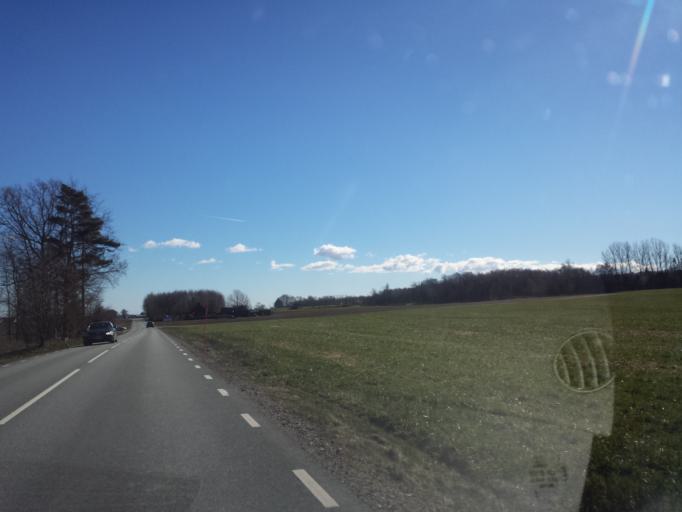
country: SE
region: Skane
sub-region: Sjobo Kommun
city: Sjoebo
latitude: 55.6131
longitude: 13.7833
